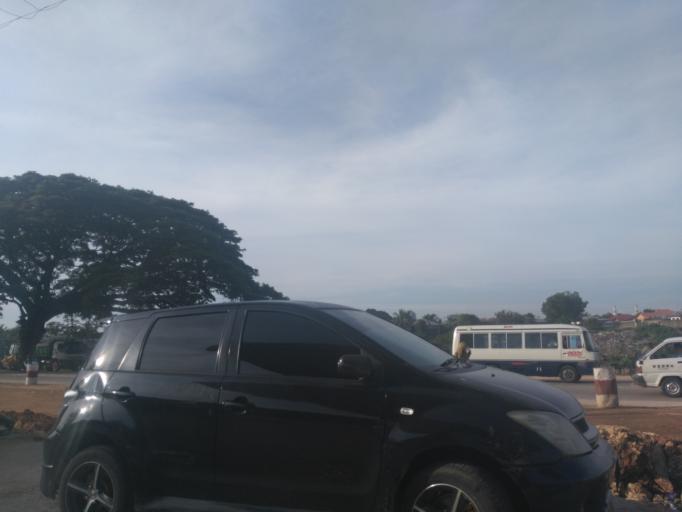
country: TZ
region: Zanzibar Urban/West
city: Zanzibar
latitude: -6.1785
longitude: 39.2283
